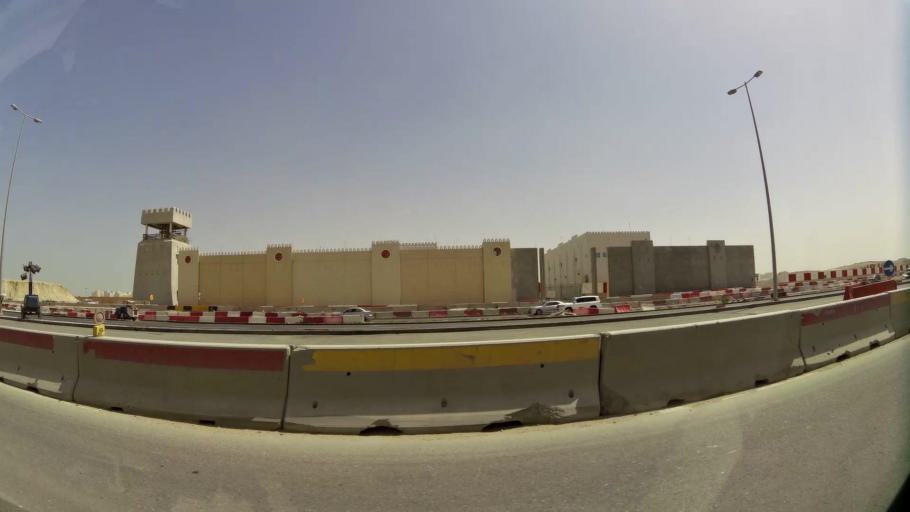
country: QA
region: Baladiyat Umm Salal
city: Umm Salal Muhammad
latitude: 25.3709
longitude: 51.4586
